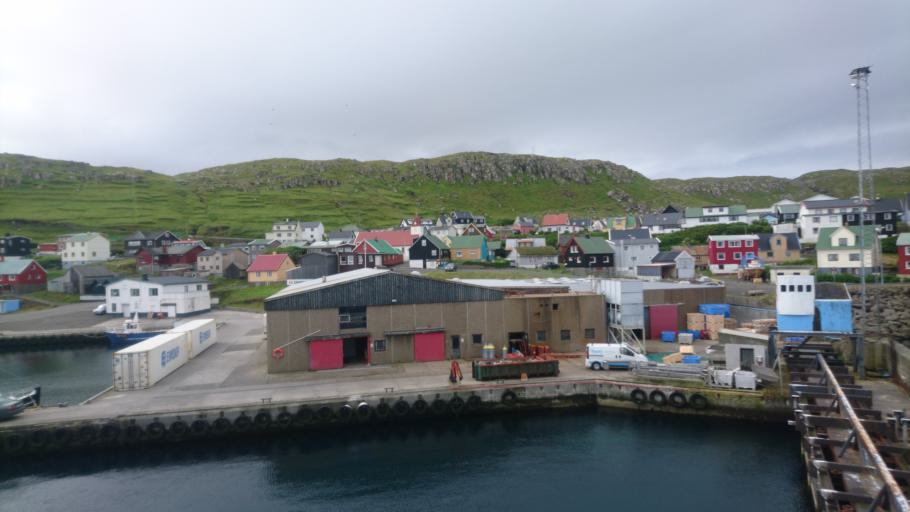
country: FO
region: Sandoy
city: Sandur
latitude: 61.9037
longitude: -6.8799
